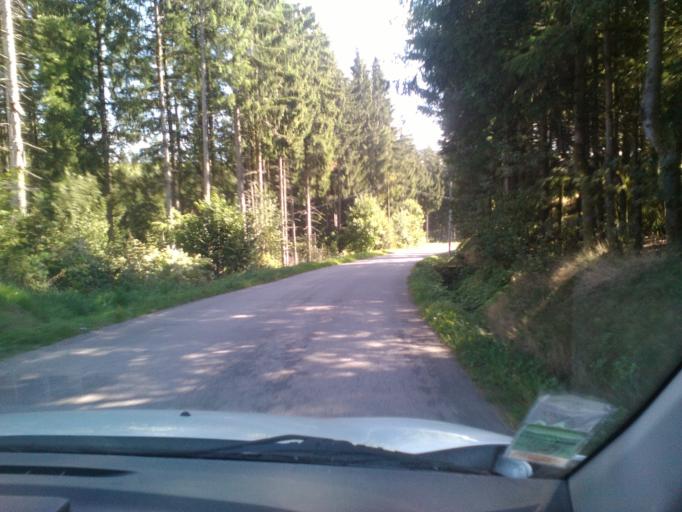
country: FR
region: Lorraine
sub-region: Departement des Vosges
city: Le Tholy
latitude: 48.0421
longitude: 6.7518
